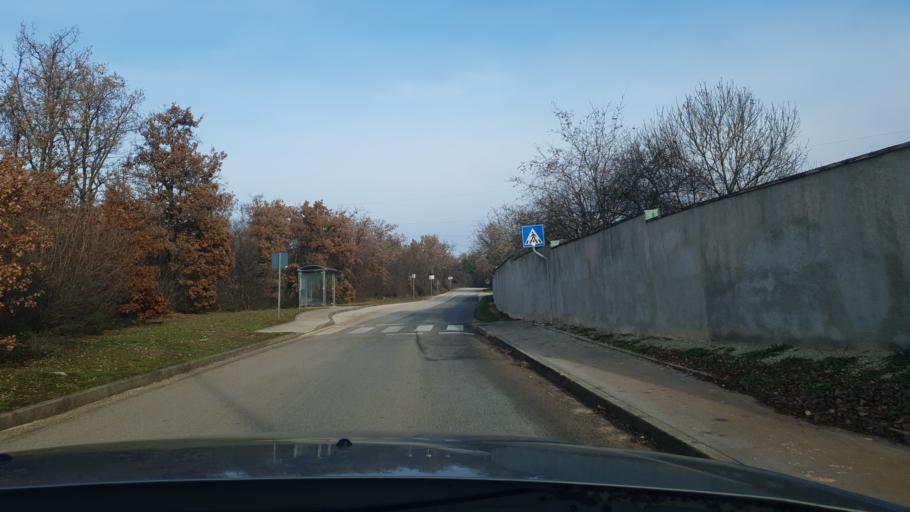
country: HR
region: Istarska
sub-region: Grad Porec
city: Porec
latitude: 45.2316
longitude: 13.6257
